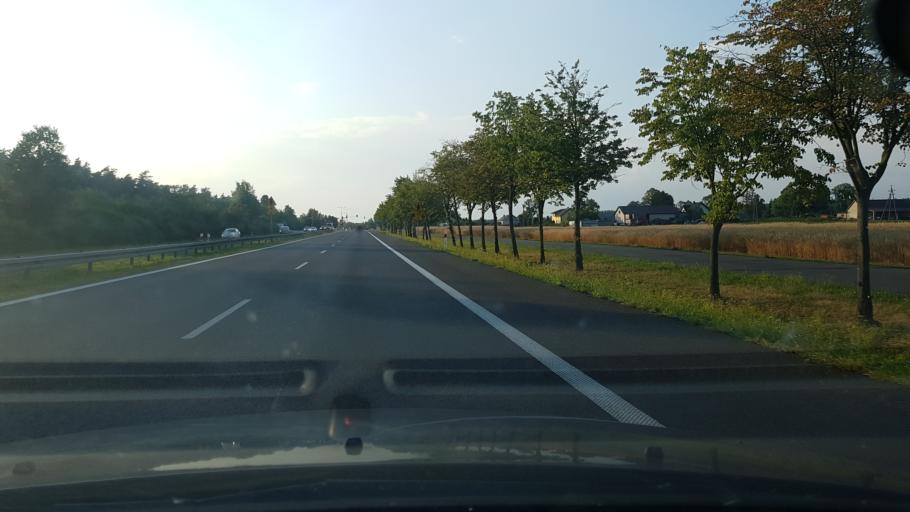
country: PL
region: Masovian Voivodeship
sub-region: Powiat plonski
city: Zaluski
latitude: 52.4952
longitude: 20.5427
